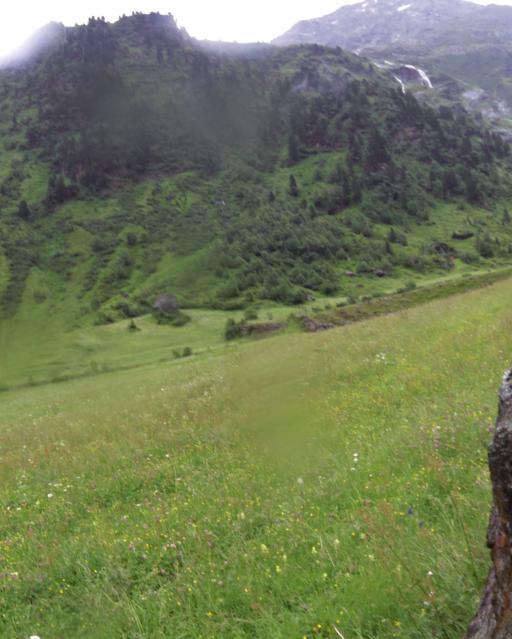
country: AT
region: Tyrol
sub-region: Politischer Bezirk Innsbruck Land
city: Neustift im Stubaital
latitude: 47.0126
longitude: 11.2253
